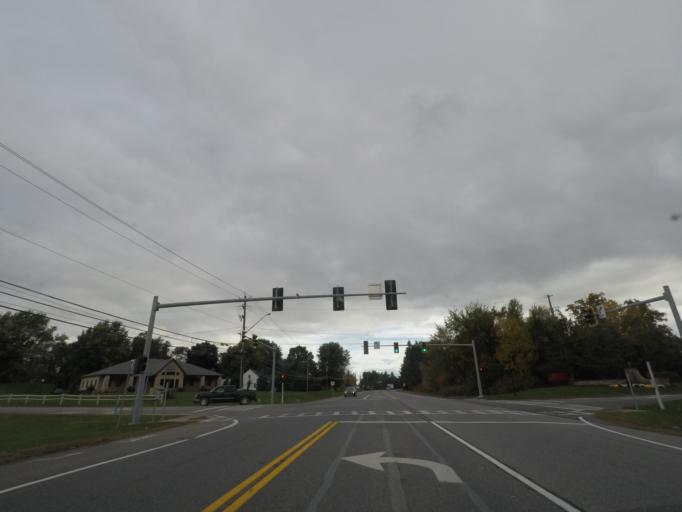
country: US
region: New York
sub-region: Saratoga County
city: Mechanicville
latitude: 42.8794
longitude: -73.7224
